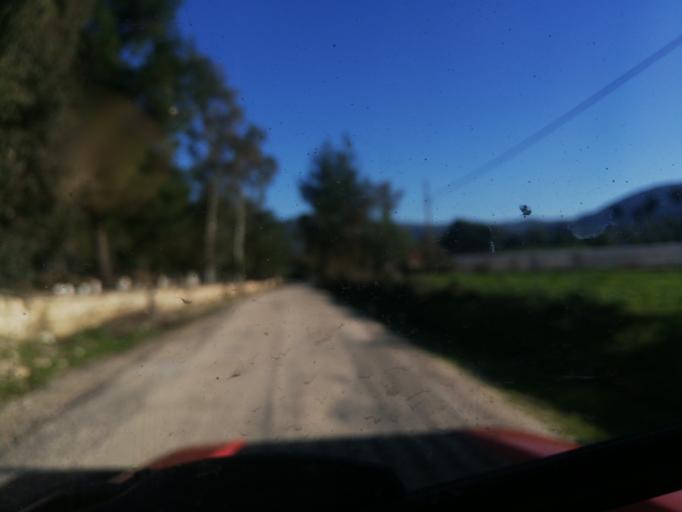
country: TR
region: Antalya
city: Kas
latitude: 36.2852
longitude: 29.7059
